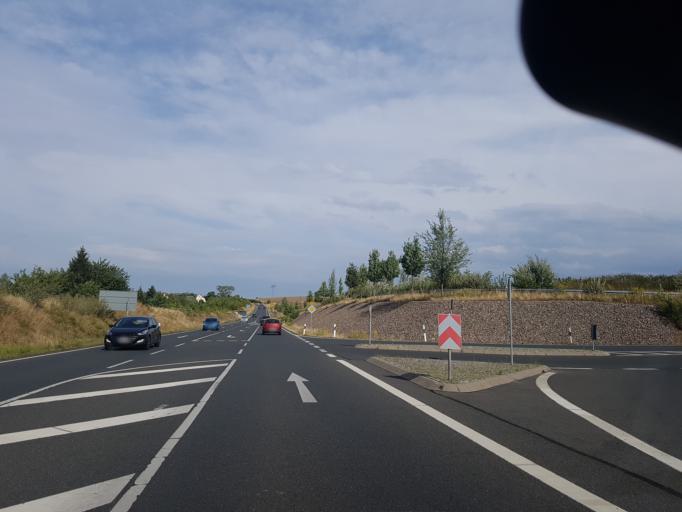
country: DE
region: Saxony
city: Dobeln
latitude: 51.1238
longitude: 13.0768
